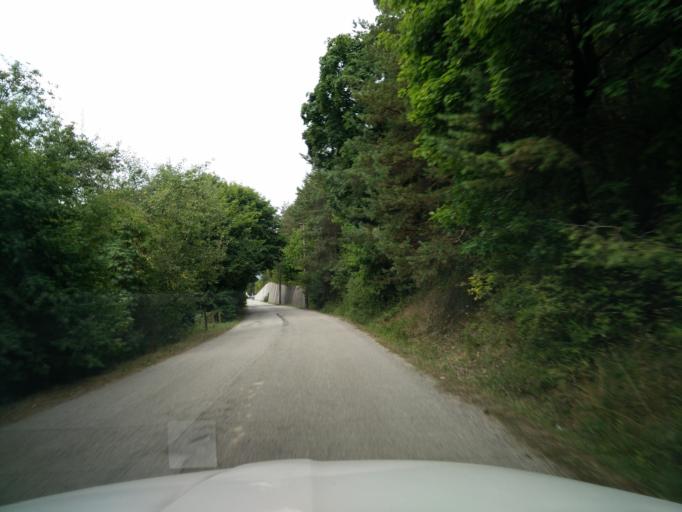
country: SK
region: Nitriansky
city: Novaky
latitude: 48.7266
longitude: 18.5369
